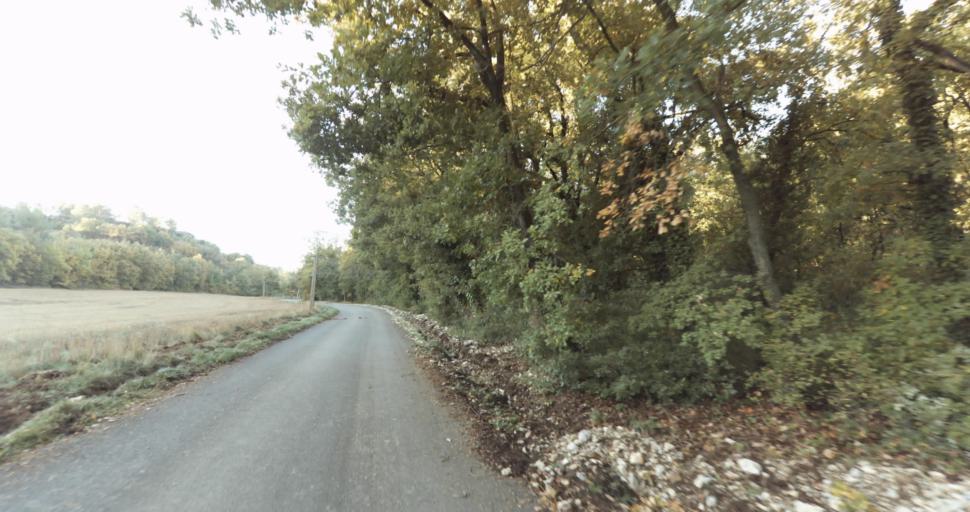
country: FR
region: Provence-Alpes-Cote d'Azur
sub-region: Departement des Bouches-du-Rhone
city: Venelles
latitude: 43.5959
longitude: 5.5179
